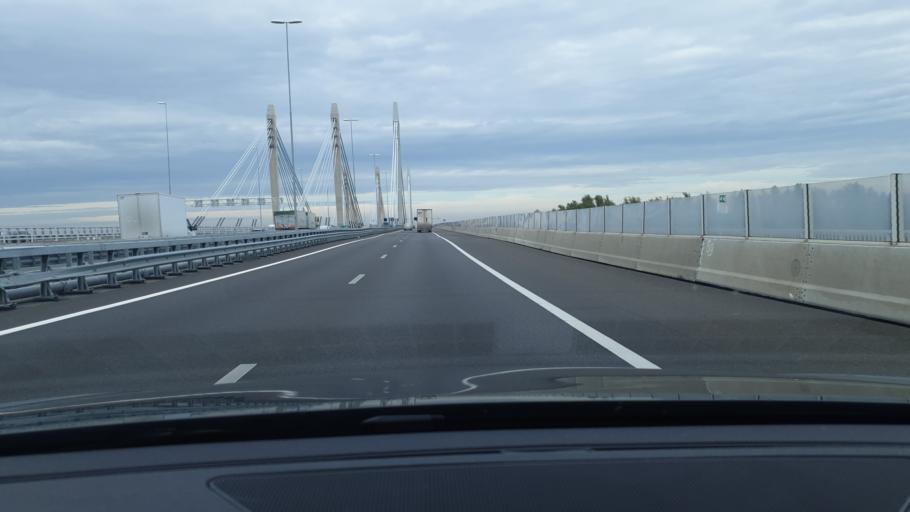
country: NL
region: Gelderland
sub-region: Gemeente Overbetuwe
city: Andelst
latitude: 51.8806
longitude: 5.7374
